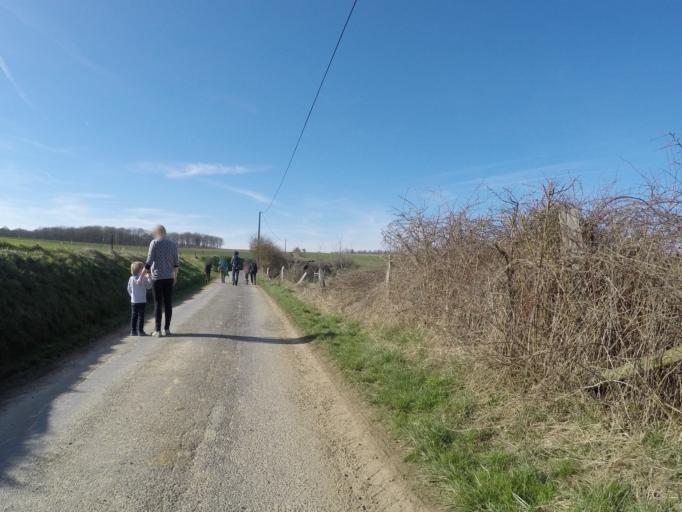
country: BE
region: Wallonia
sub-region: Province de Namur
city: Hamois
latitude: 50.3386
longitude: 5.1436
